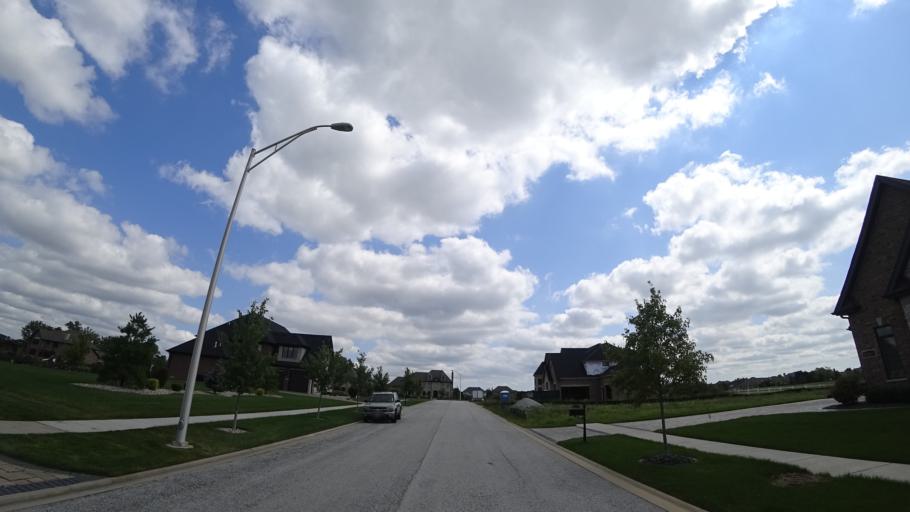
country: US
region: Illinois
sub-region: Cook County
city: Orland Hills
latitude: 41.5722
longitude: -87.8781
